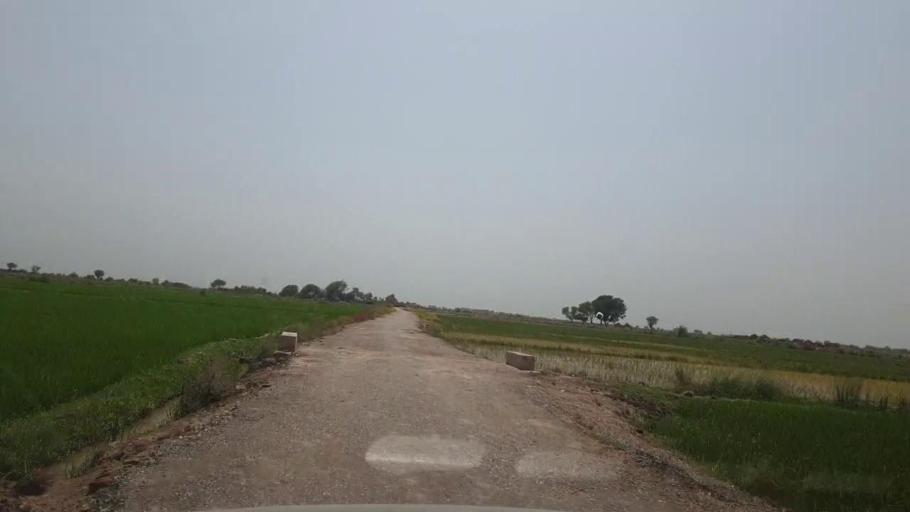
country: PK
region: Sindh
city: Garhi Yasin
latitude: 28.0589
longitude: 68.3172
